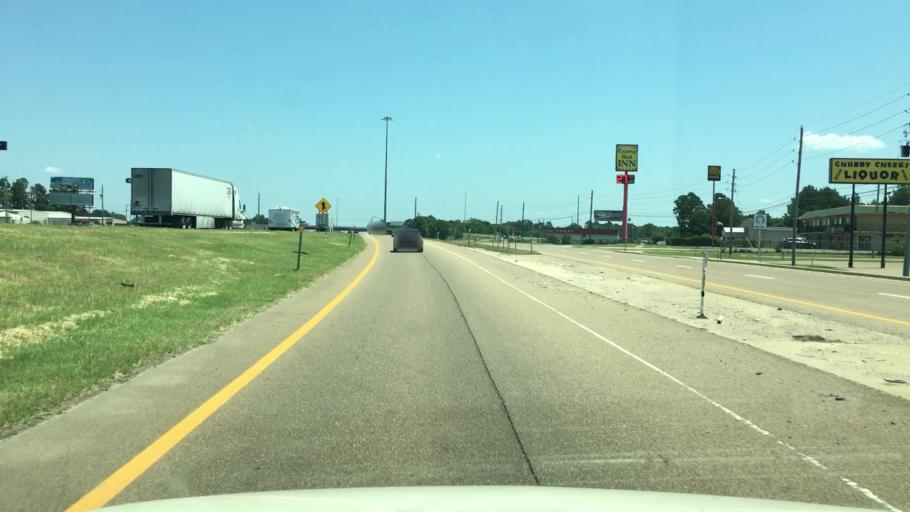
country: US
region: Arkansas
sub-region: Miller County
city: Texarkana
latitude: 33.4700
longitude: -94.0345
